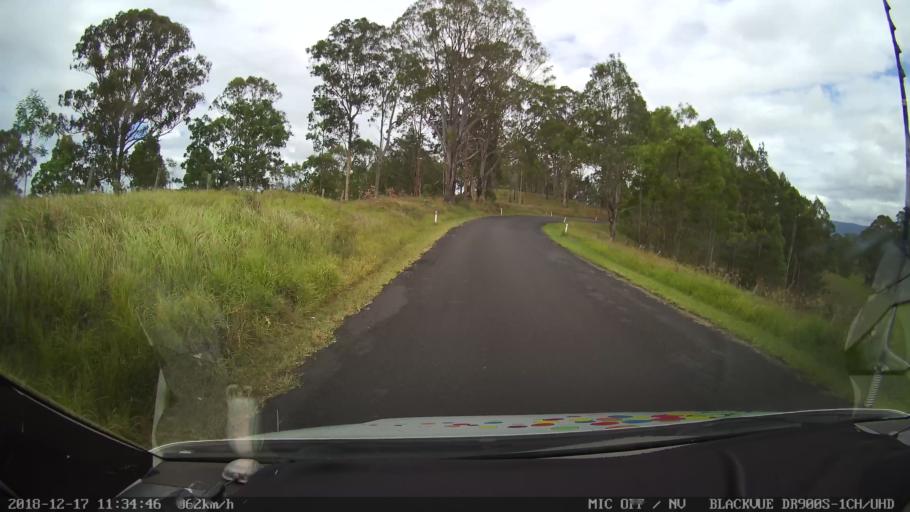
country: AU
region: New South Wales
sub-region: Kyogle
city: Kyogle
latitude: -28.7258
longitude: 152.6104
